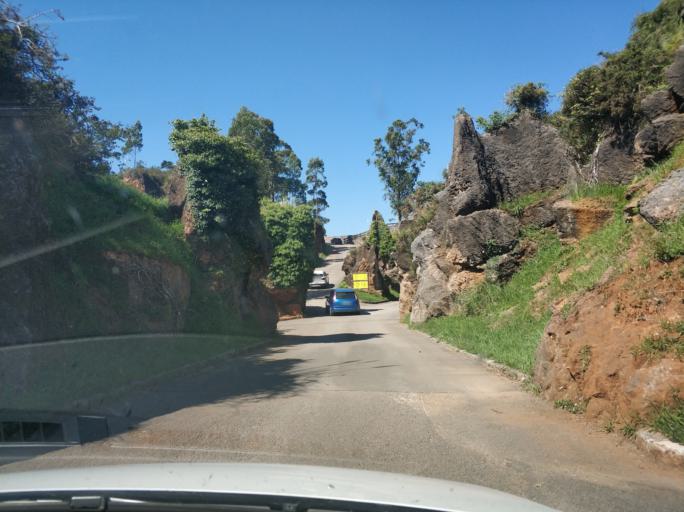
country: ES
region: Cantabria
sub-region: Provincia de Cantabria
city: Penagos
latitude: 43.3636
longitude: -3.8366
